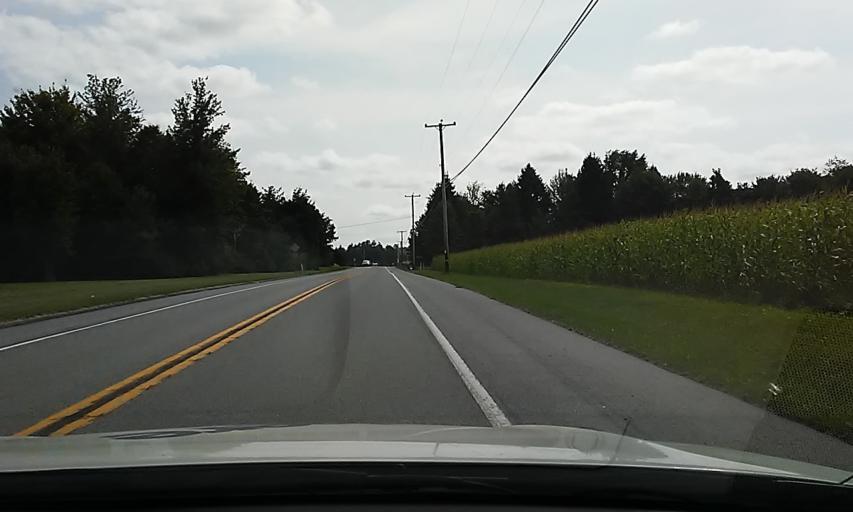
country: US
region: Pennsylvania
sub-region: Jefferson County
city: Punxsutawney
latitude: 40.8910
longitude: -79.0182
